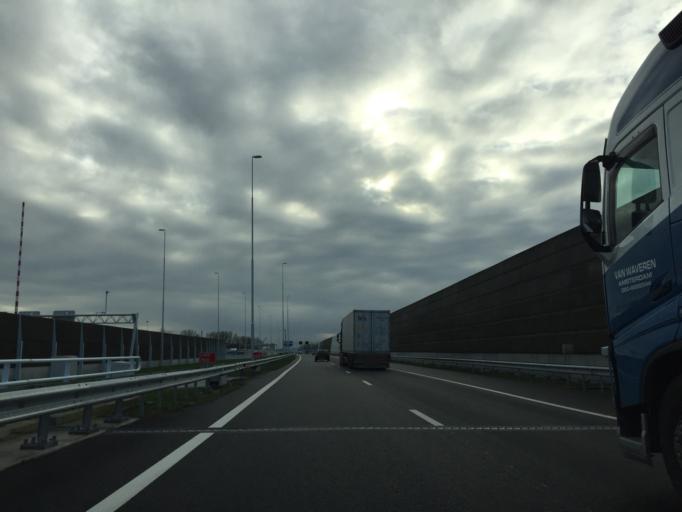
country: NL
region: South Holland
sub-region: Gemeente Schiedam
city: Schiedam
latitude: 51.9274
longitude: 4.3649
